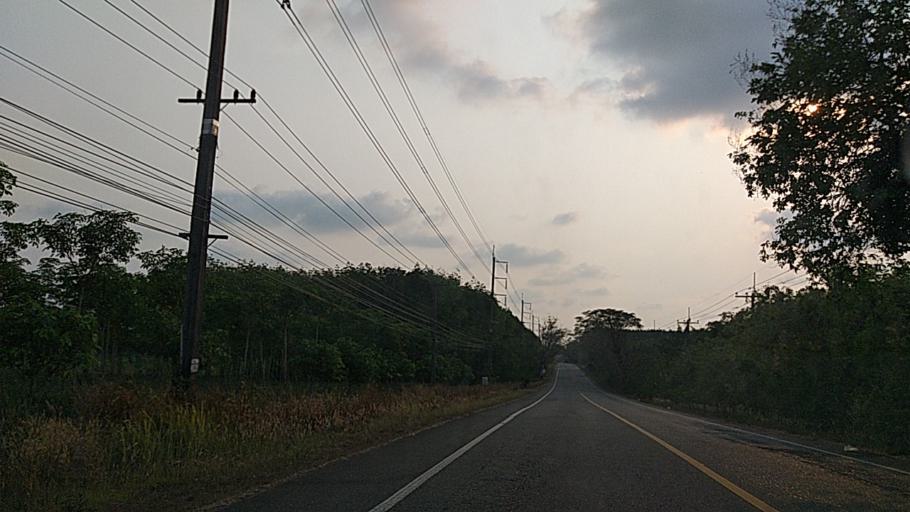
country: TH
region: Trat
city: Laem Ngop
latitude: 12.2633
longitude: 102.2985
